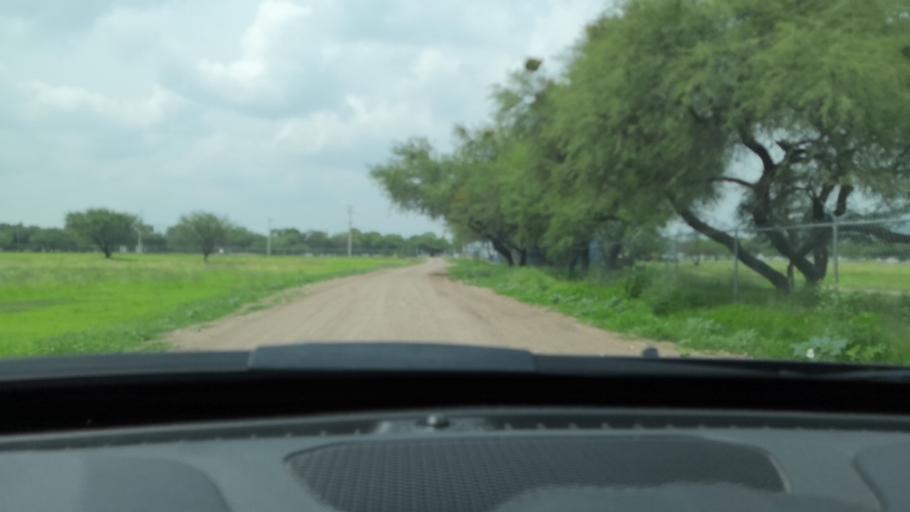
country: MX
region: Guanajuato
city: Leon
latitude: 21.1906
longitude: -101.6832
